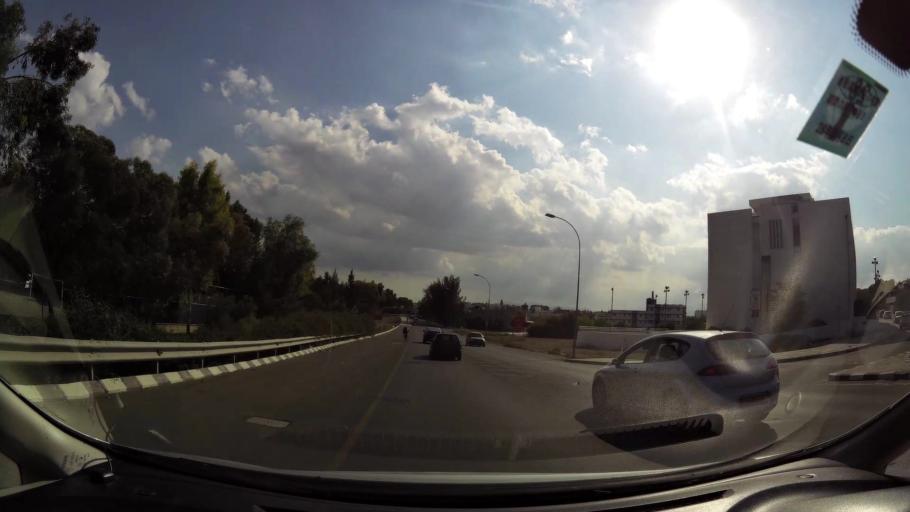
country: CY
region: Lefkosia
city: Nicosia
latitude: 35.1613
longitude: 33.3113
